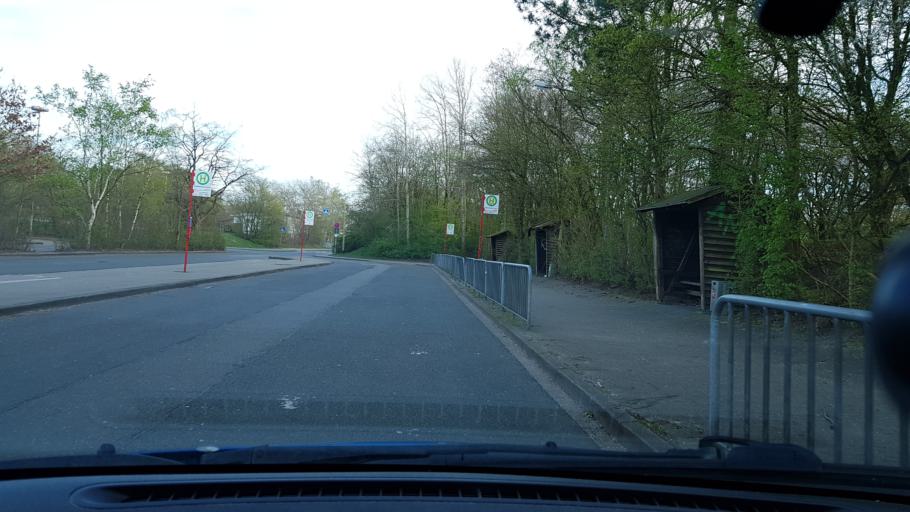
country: DE
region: Lower Saxony
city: Buchholz in der Nordheide
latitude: 53.3234
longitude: 9.8411
